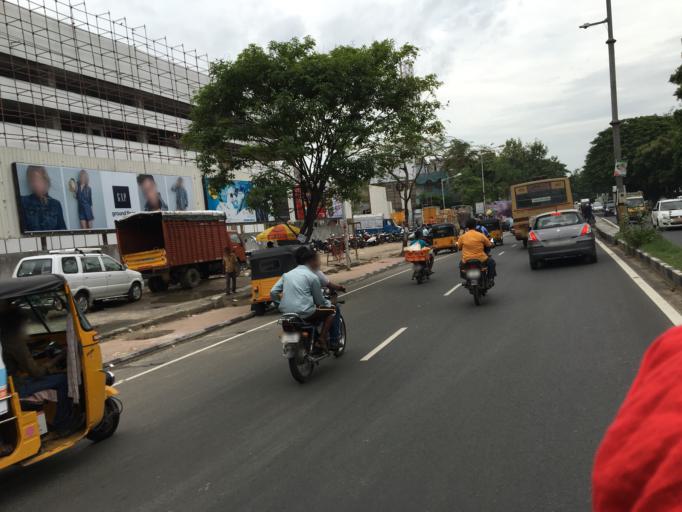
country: IN
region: Tamil Nadu
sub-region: Kancheepuram
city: Alandur
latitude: 12.9933
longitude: 80.2183
